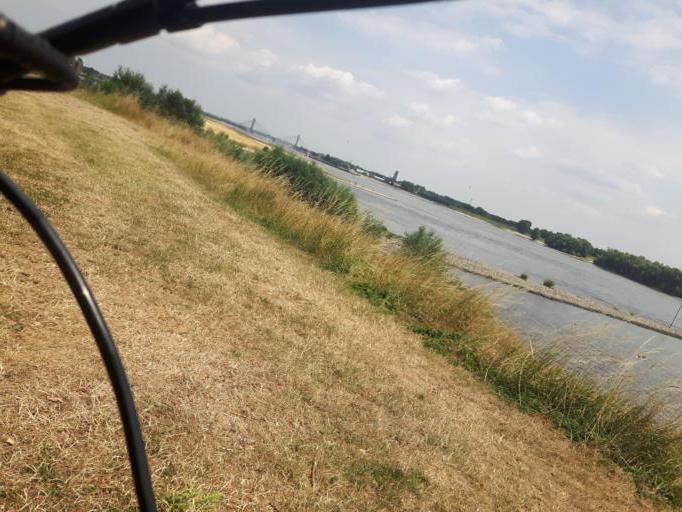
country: NL
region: Gelderland
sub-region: Gemeente Zaltbommel
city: Zaltbommel
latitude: 51.8122
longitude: 5.2150
